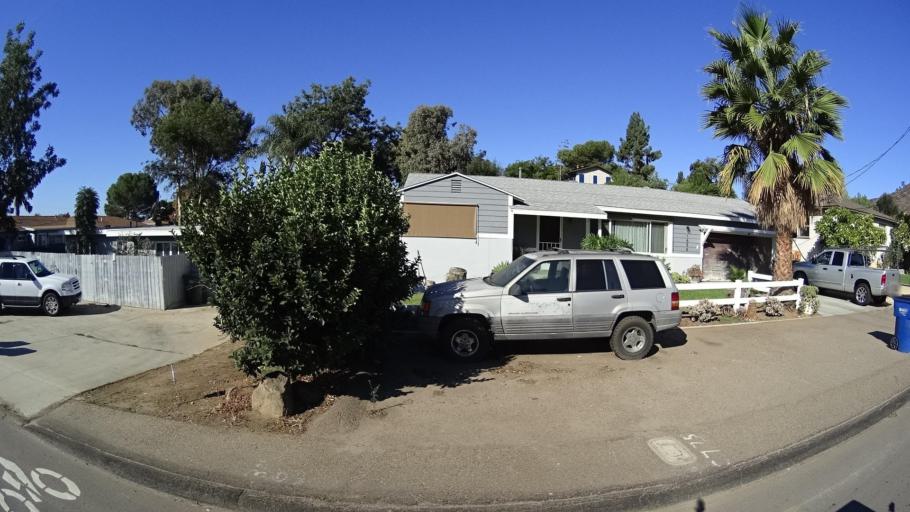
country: US
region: California
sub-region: San Diego County
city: Bostonia
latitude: 32.8179
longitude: -116.9358
